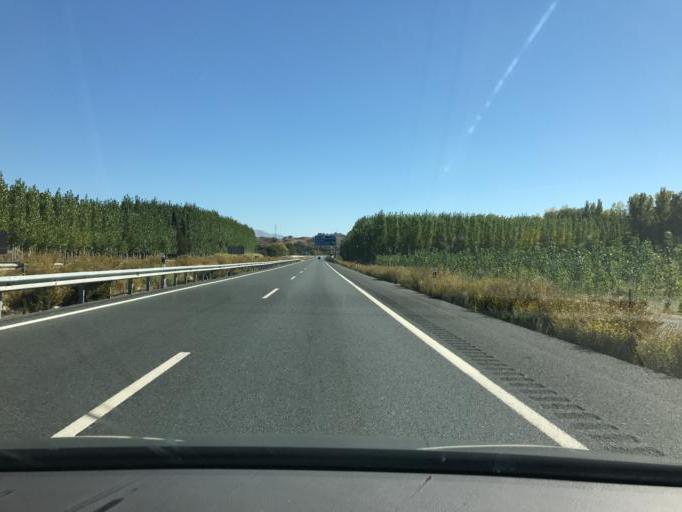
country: ES
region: Andalusia
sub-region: Provincia de Granada
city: Purullena
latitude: 37.3284
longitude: -3.2131
